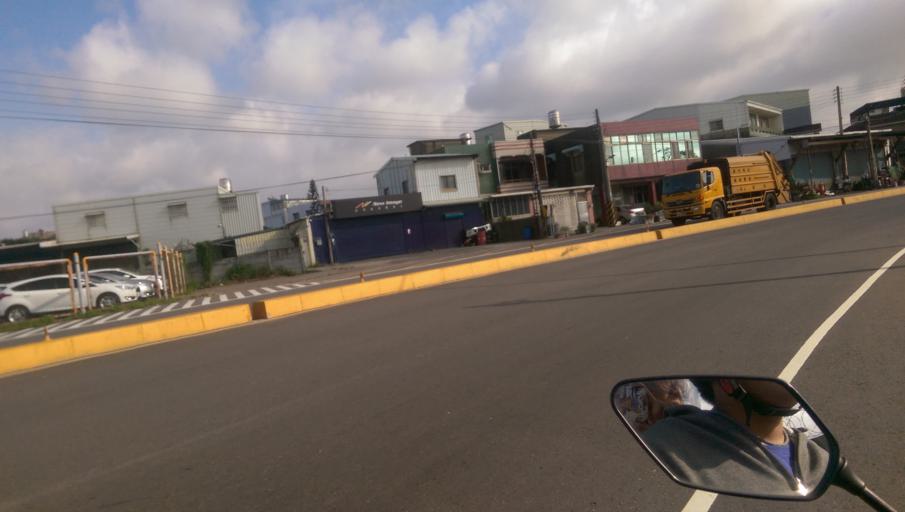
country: TW
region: Taiwan
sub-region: Hsinchu
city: Hsinchu
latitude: 24.8310
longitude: 120.9554
